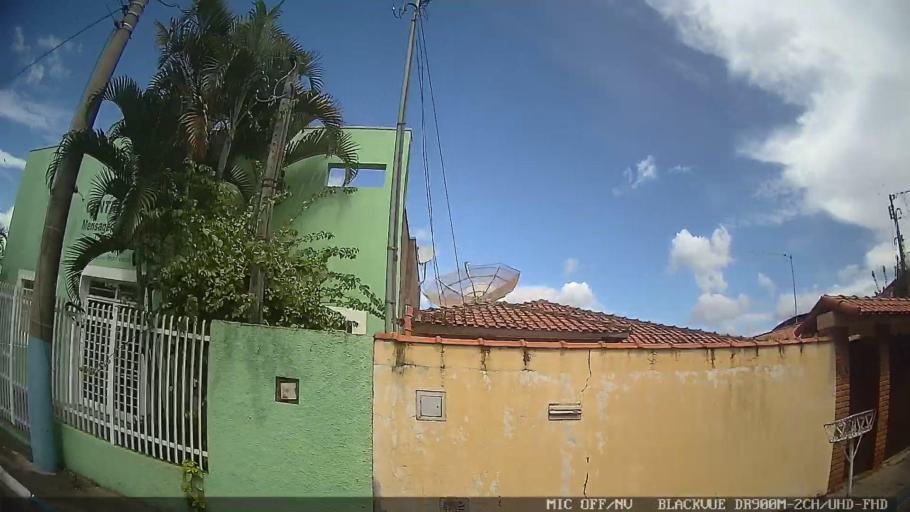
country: BR
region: Sao Paulo
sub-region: Conchas
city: Conchas
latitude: -23.0197
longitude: -48.0095
